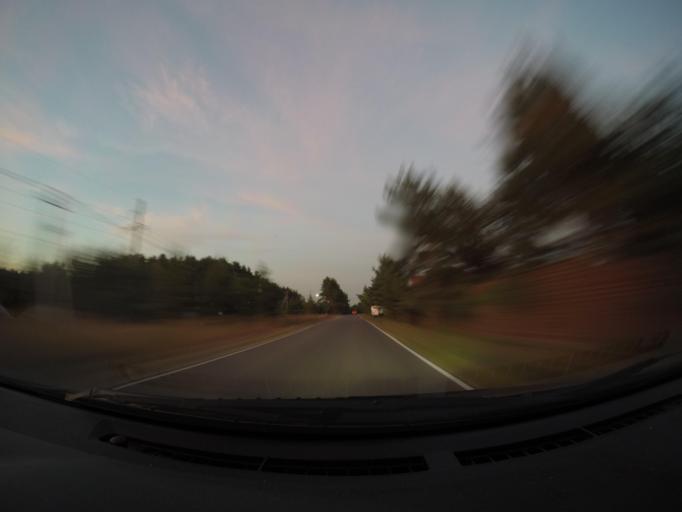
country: RU
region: Moskovskaya
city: Rechitsy
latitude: 55.5433
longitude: 38.4405
